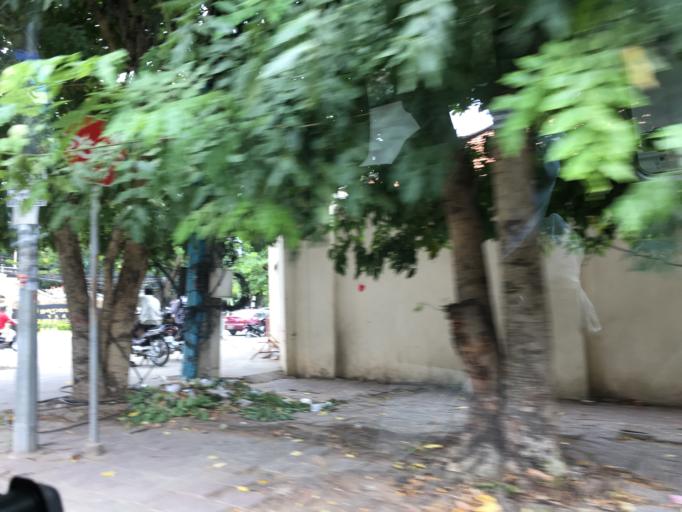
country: KH
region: Phnom Penh
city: Phnom Penh
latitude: 11.5386
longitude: 104.9280
